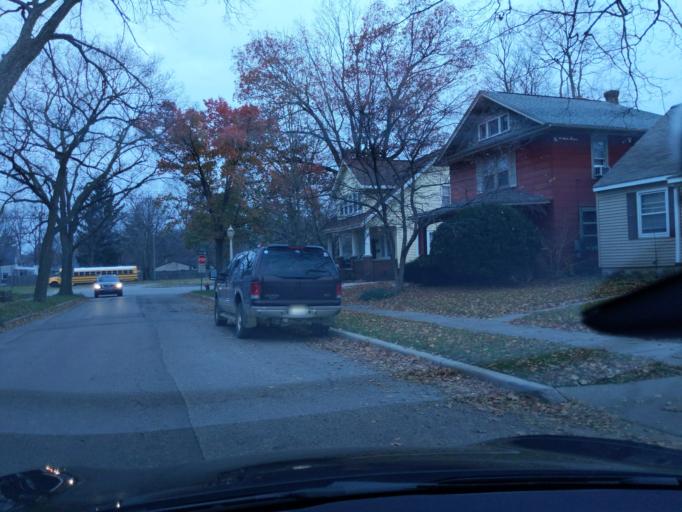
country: US
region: Michigan
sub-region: Ingham County
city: Lansing
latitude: 42.7178
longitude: -84.5666
